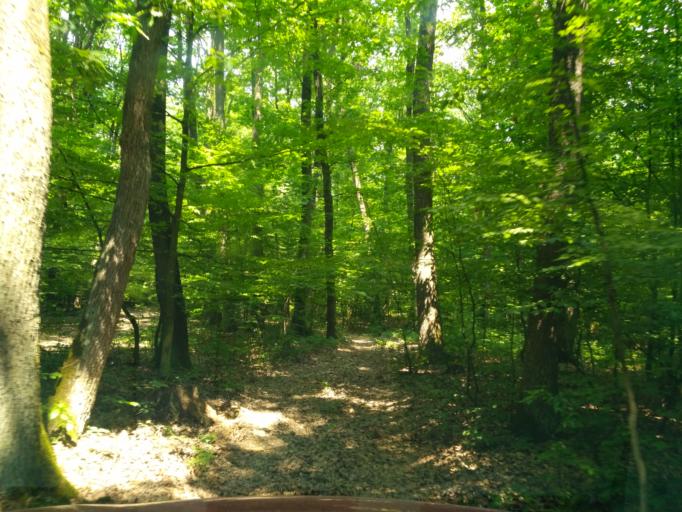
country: SK
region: Kosicky
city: Moldava nad Bodvou
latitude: 48.6394
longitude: 21.0394
